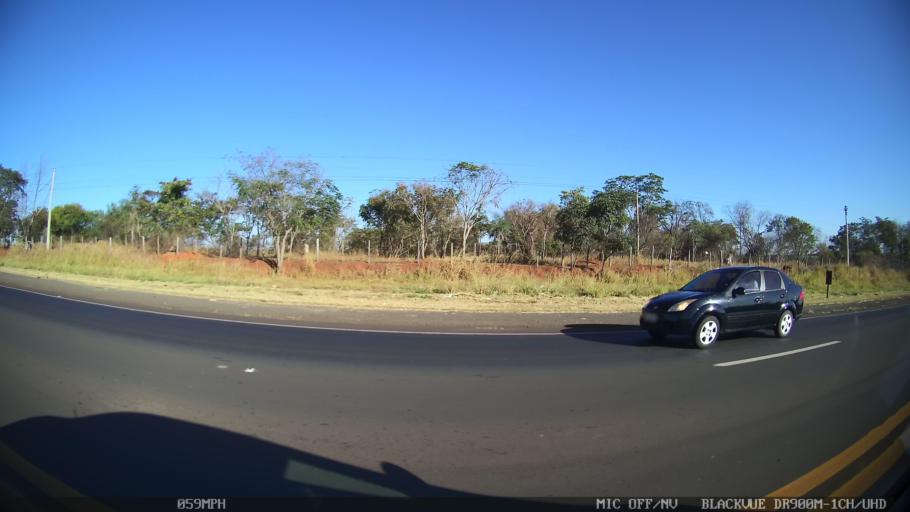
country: BR
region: Sao Paulo
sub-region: Olimpia
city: Olimpia
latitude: -20.7047
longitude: -48.9516
